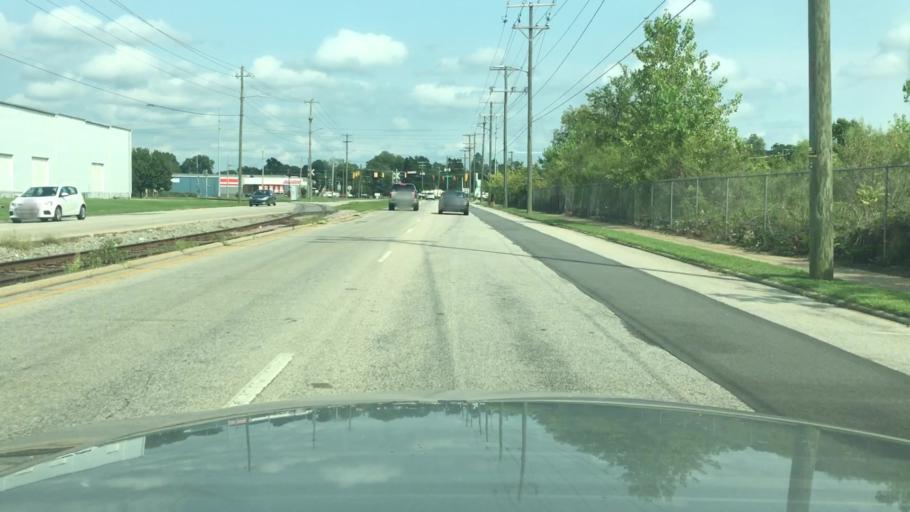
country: US
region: North Carolina
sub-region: Cumberland County
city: Fayetteville
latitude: 35.0466
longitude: -78.8678
